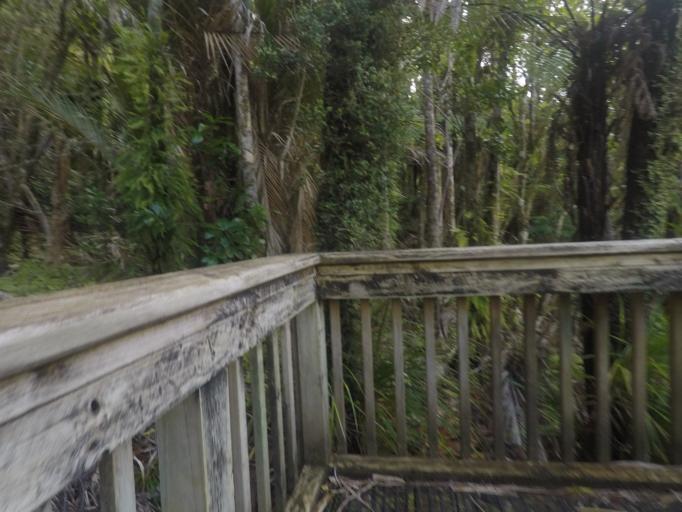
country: NZ
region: Auckland
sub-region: Auckland
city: Titirangi
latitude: -37.0016
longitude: 174.5507
